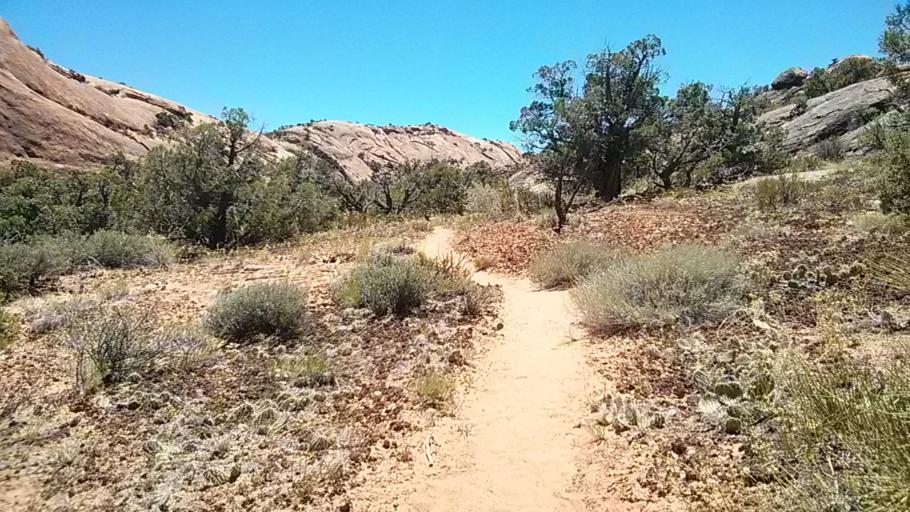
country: US
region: Utah
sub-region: Grand County
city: Moab
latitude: 38.4434
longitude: -109.9157
